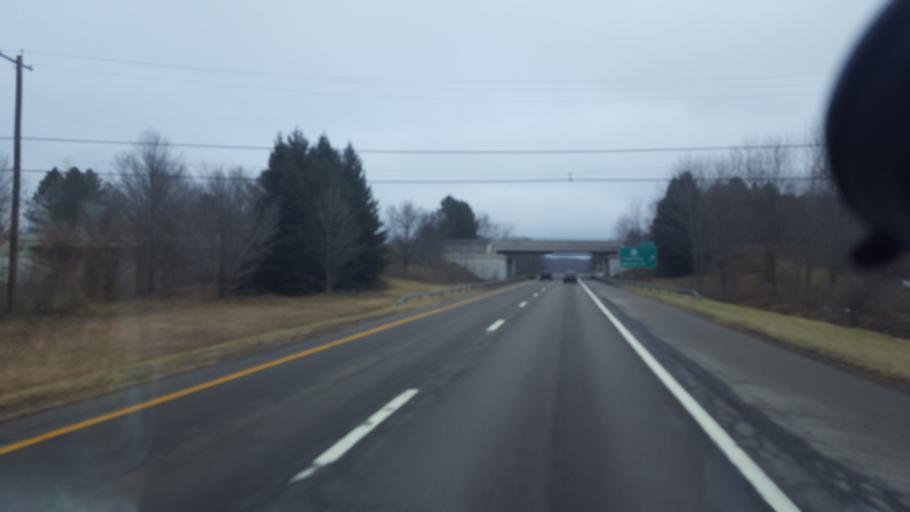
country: US
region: New York
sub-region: Chautauqua County
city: Falconer
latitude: 42.1425
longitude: -79.0941
